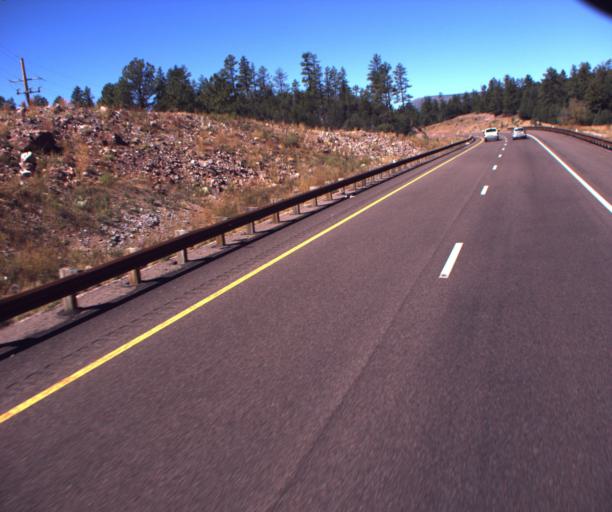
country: US
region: Arizona
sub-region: Gila County
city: Star Valley
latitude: 34.3135
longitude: -111.0517
